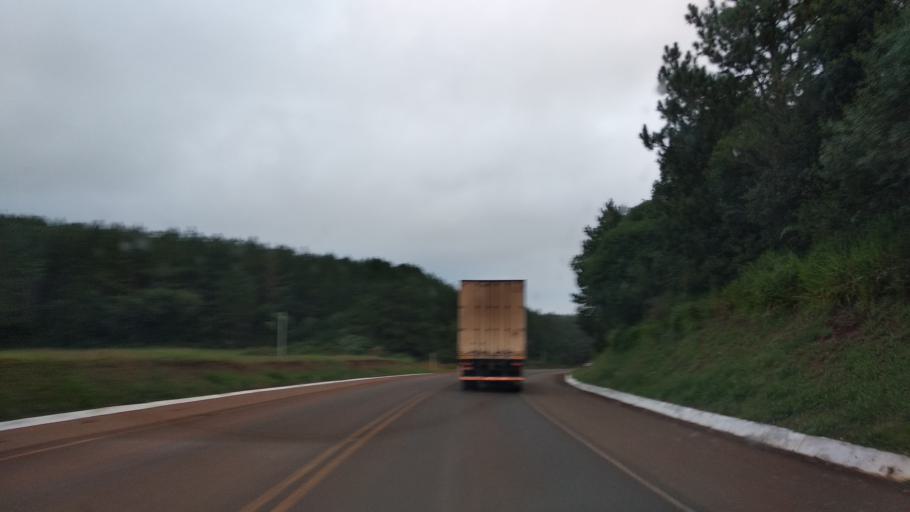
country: BR
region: Santa Catarina
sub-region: Campos Novos
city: Campos Novos
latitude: -27.3988
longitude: -51.0404
